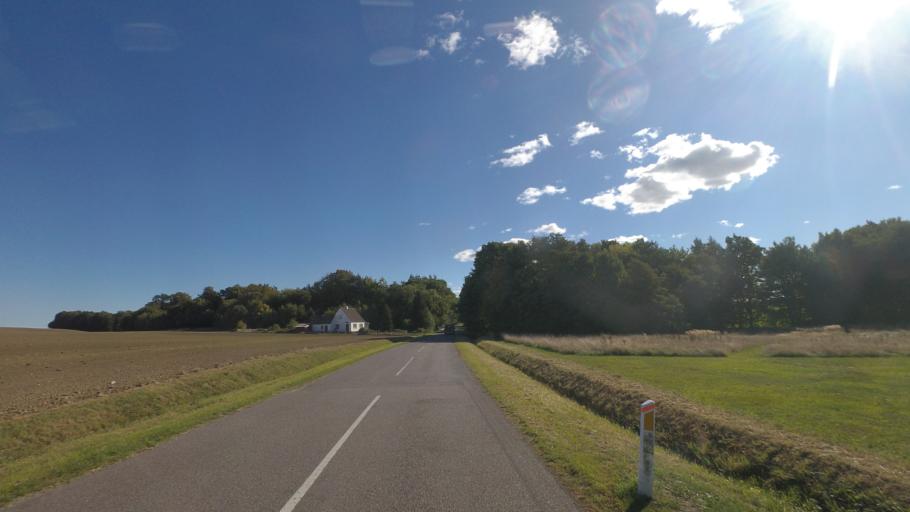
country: DK
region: Capital Region
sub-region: Bornholm Kommune
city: Akirkeby
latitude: 55.1335
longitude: 15.0212
